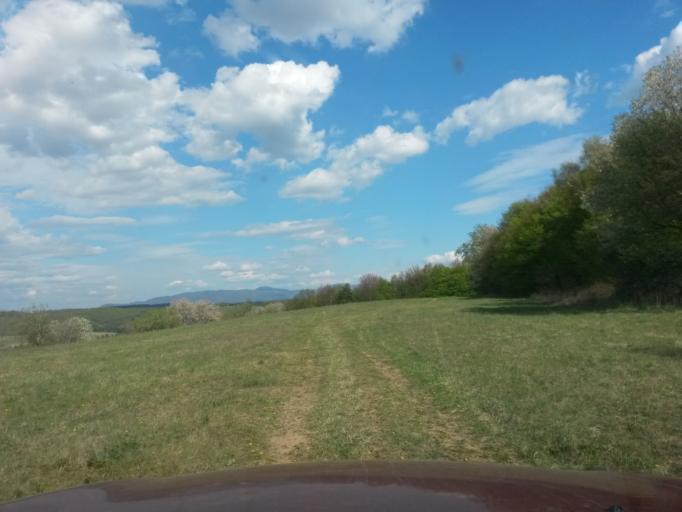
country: SK
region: Presovsky
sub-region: Okres Presov
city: Presov
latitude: 48.9501
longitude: 21.1469
